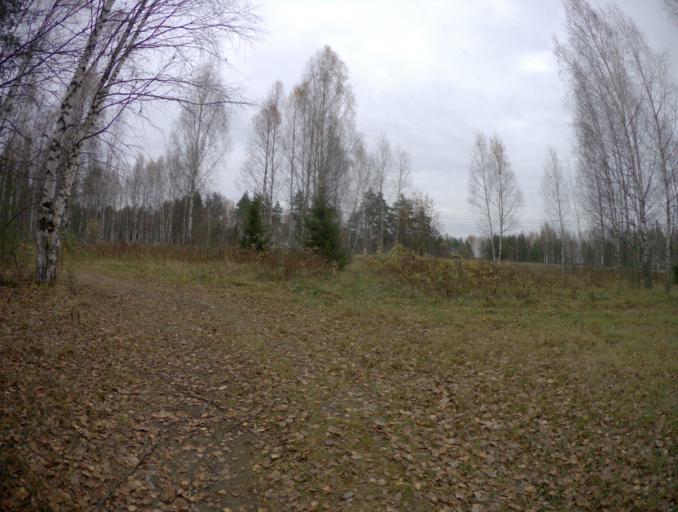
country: RU
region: Vladimir
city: Krasnyy Oktyabr'
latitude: 56.0266
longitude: 38.8746
